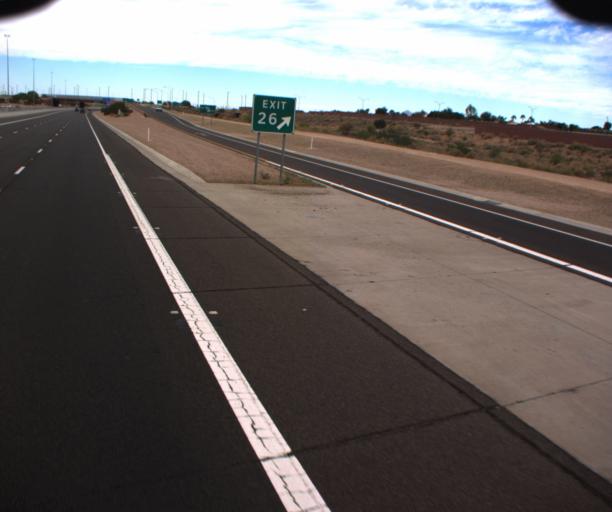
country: US
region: Arizona
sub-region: Pinal County
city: Apache Junction
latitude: 33.4342
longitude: -111.6445
